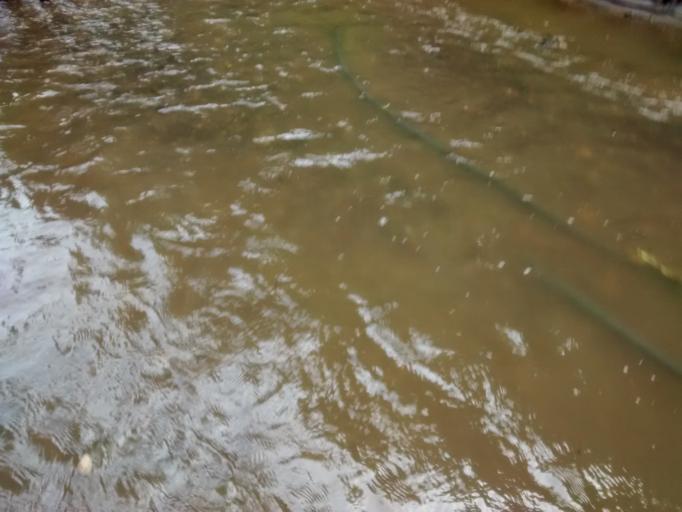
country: GT
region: Sacatepequez
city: Santo Domingo Xenacoj
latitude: 14.6950
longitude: -90.7333
